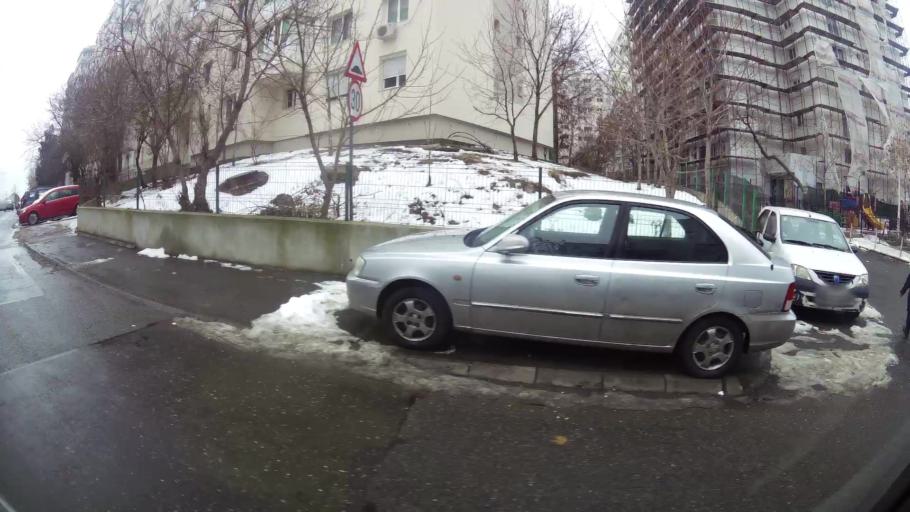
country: RO
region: Bucuresti
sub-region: Municipiul Bucuresti
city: Bucharest
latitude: 44.4146
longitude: 26.1349
